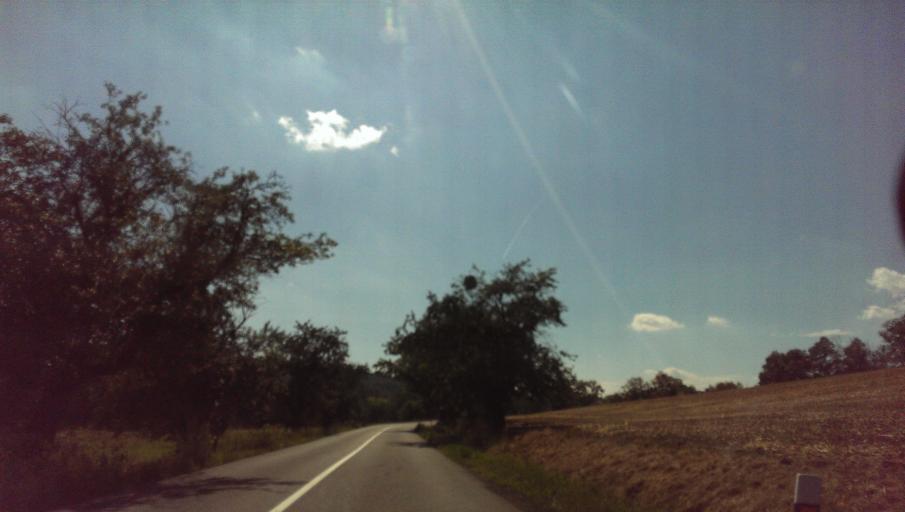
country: CZ
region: Zlin
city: Valasske Mezirici
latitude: 49.4635
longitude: 17.9279
